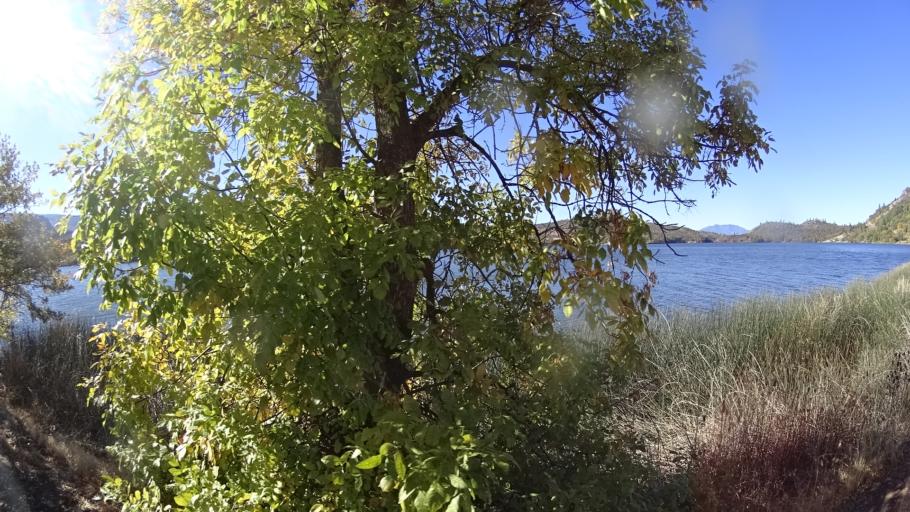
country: US
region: California
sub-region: Siskiyou County
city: Montague
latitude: 41.9874
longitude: -122.3083
